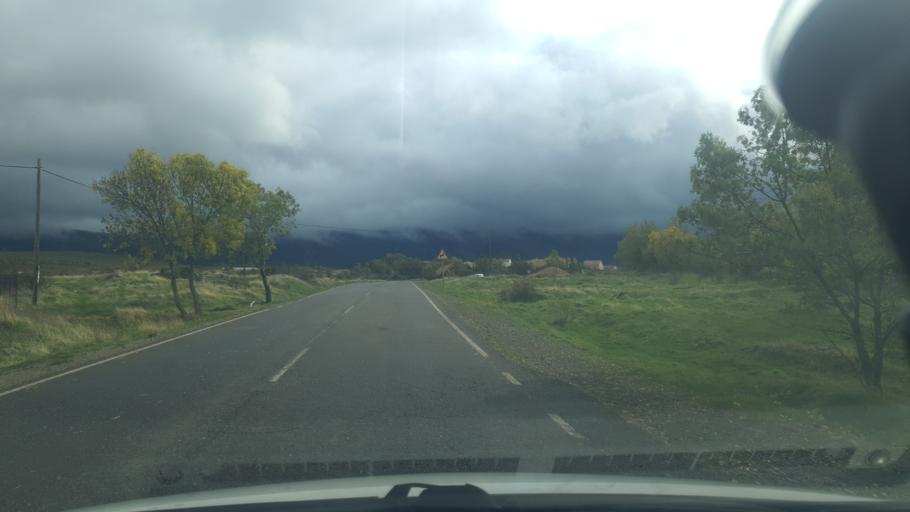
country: ES
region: Castille and Leon
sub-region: Provincia de Segovia
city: Gallegos
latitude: 41.0794
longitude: -3.7877
